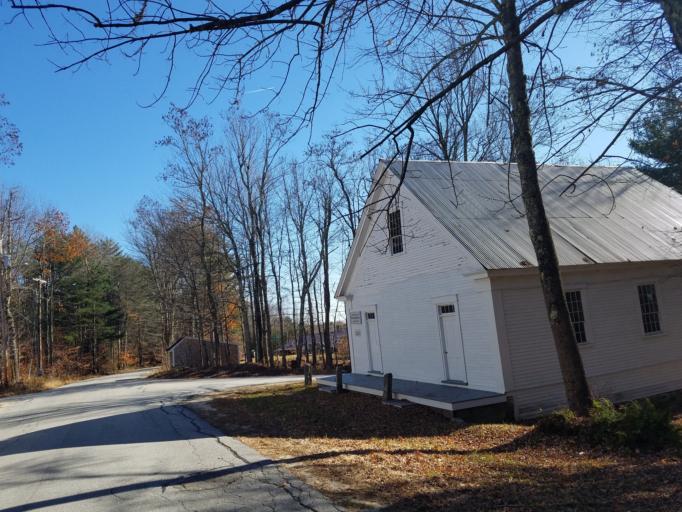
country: US
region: New Hampshire
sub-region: Carroll County
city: Effingham
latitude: 43.6793
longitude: -71.0286
